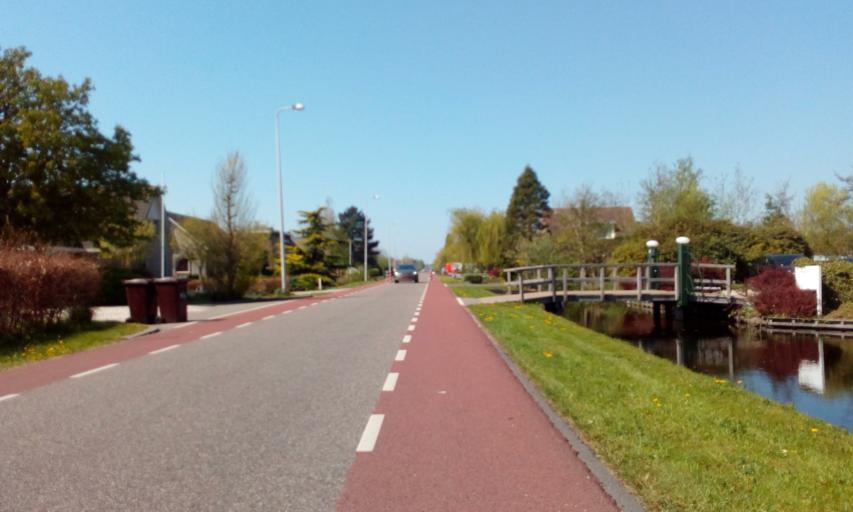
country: NL
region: South Holland
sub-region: Gemeente Boskoop
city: Boskoop
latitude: 52.0856
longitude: 4.6730
